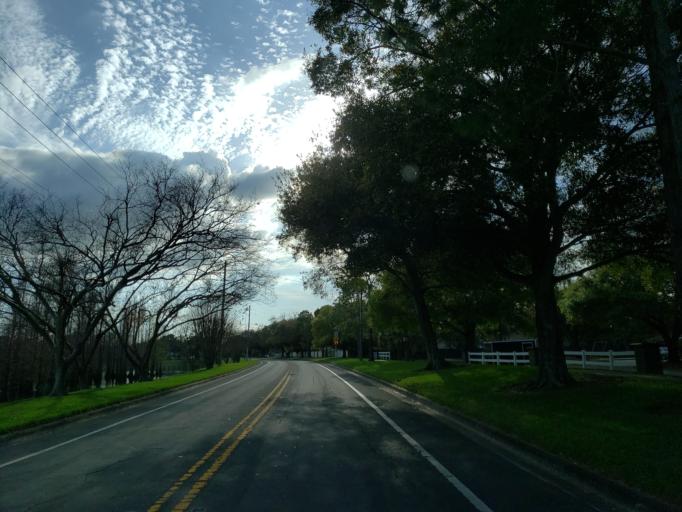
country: US
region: Florida
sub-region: Hillsborough County
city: Riverview
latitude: 27.9072
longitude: -82.3219
